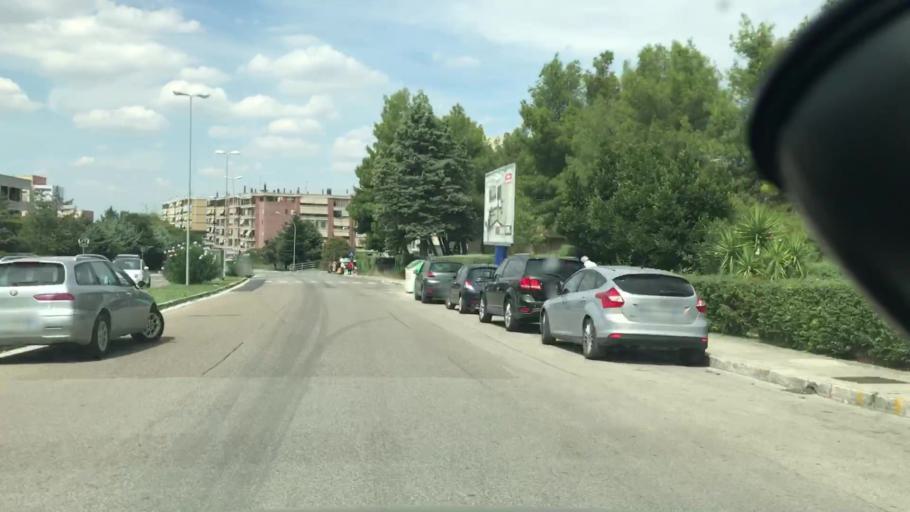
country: IT
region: Basilicate
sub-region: Provincia di Matera
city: Matera
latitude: 40.6758
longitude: 16.5836
